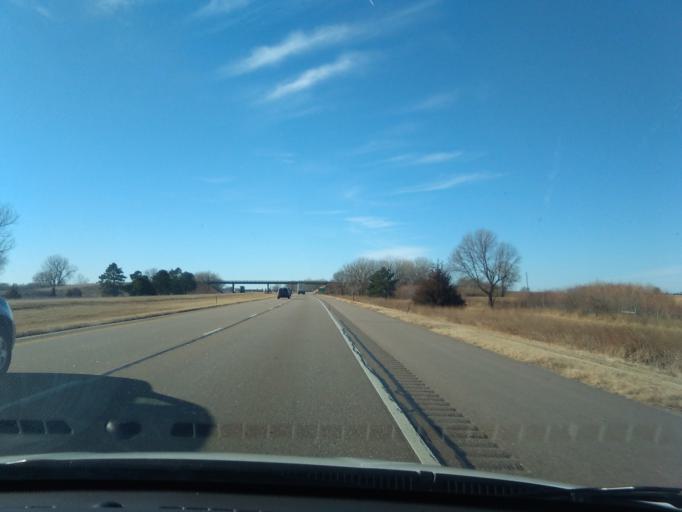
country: US
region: Nebraska
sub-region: Hall County
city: Wood River
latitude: 40.7583
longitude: -98.6029
